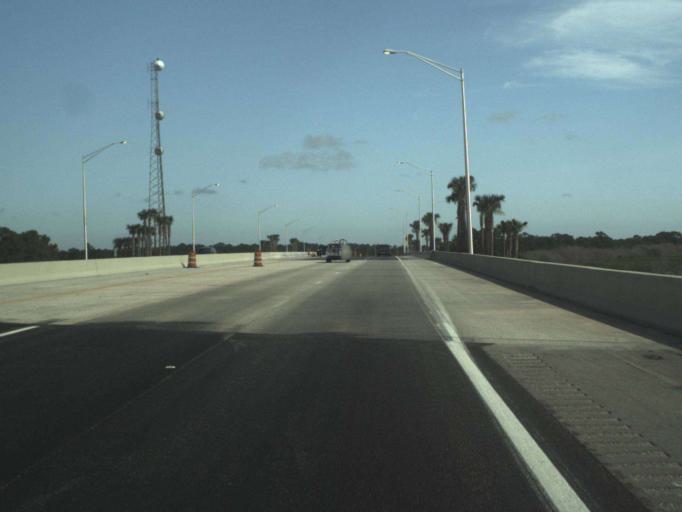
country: US
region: Florida
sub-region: Indian River County
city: West Vero Corridor
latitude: 27.6093
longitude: -80.5112
